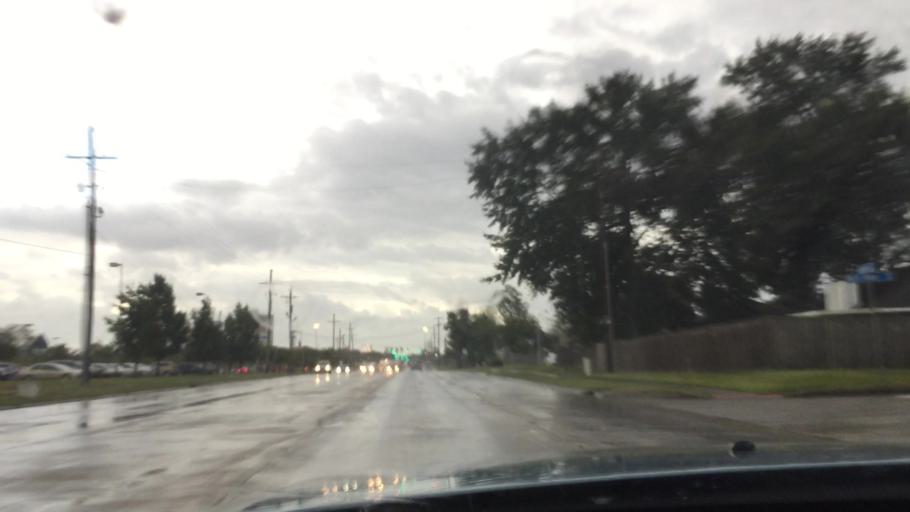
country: US
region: Louisiana
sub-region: East Baton Rouge Parish
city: Monticello
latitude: 30.4463
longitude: -91.0245
